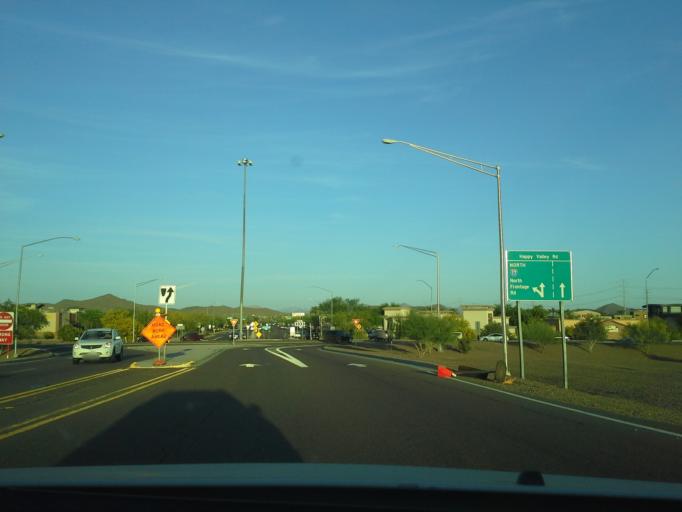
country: US
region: Arizona
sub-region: Maricopa County
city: Anthem
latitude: 33.7129
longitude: -112.1160
